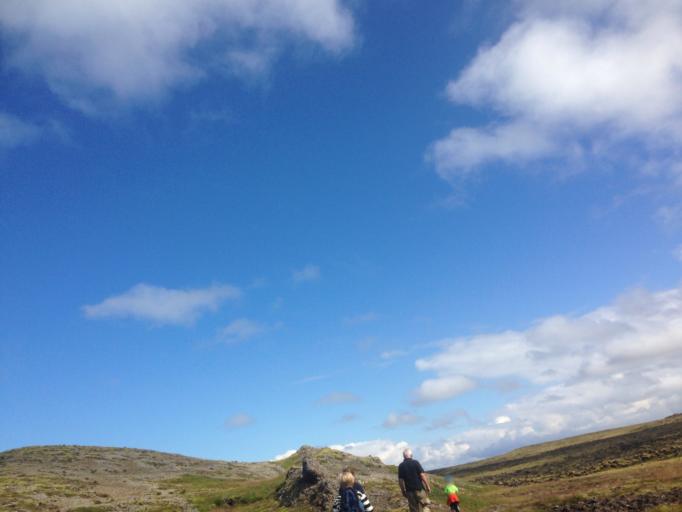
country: IS
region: Capital Region
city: Alftanes
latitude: 63.9541
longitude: -22.0797
